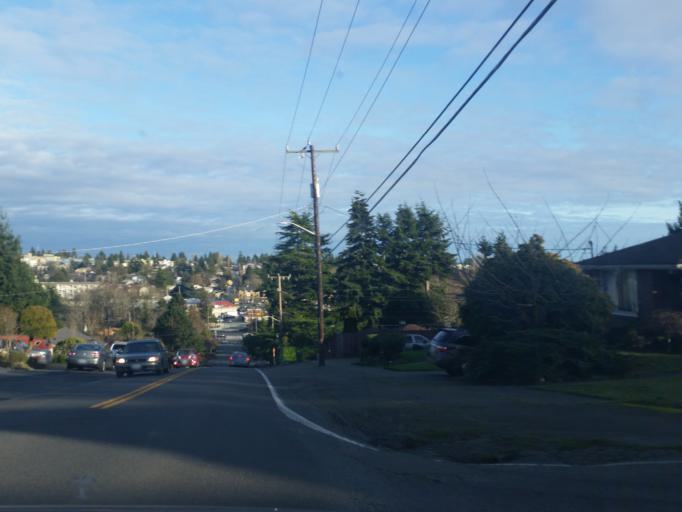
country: US
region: Washington
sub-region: King County
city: Shoreline
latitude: 47.7015
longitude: -122.3702
